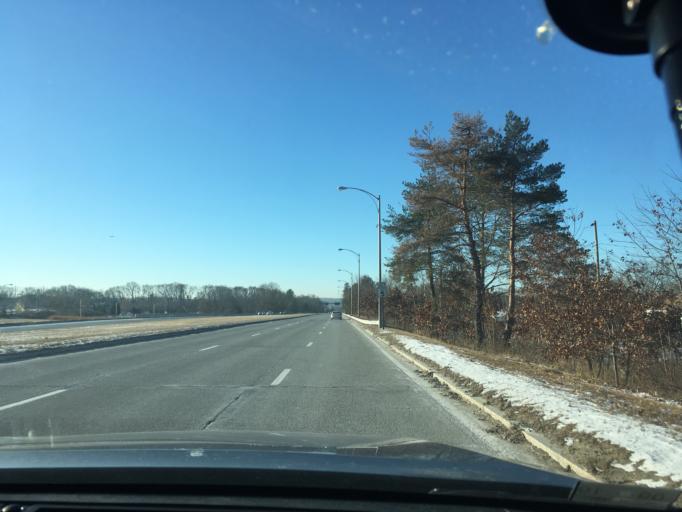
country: US
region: Rhode Island
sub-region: Providence County
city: Cranston
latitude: 41.7440
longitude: -71.4721
